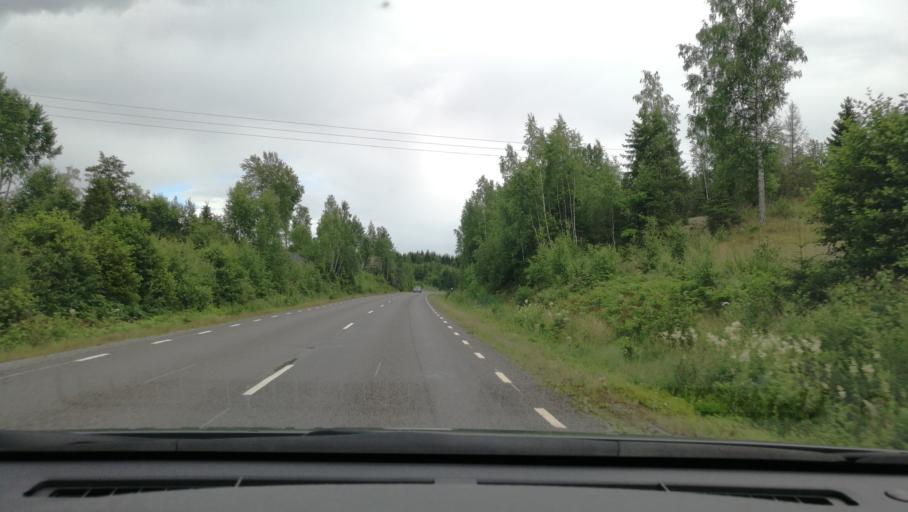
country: SE
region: OEstergoetland
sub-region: Norrkopings Kommun
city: Svartinge
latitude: 58.7868
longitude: 15.9635
